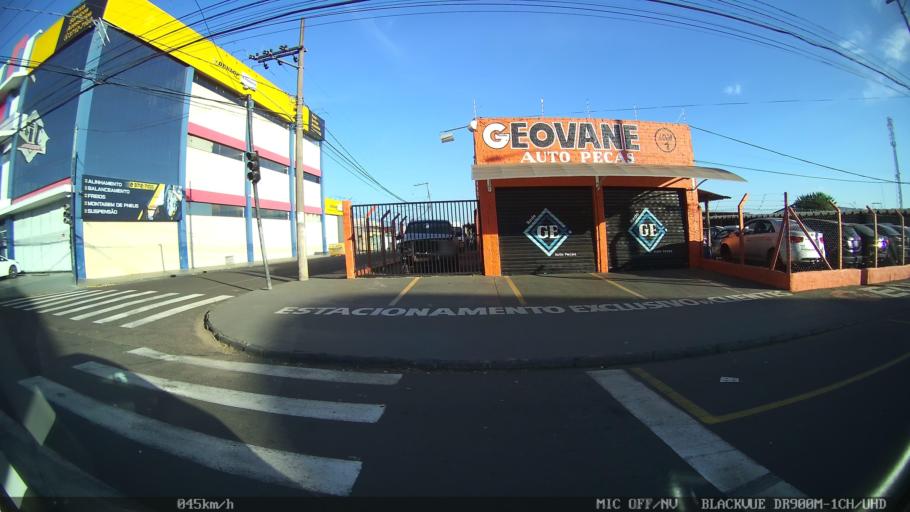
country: BR
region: Sao Paulo
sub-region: Franca
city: Franca
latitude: -20.5261
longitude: -47.3744
